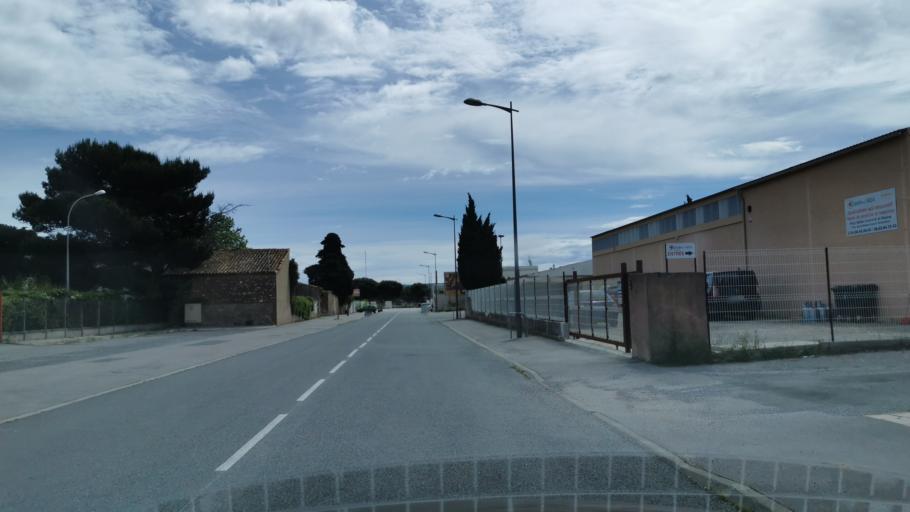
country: FR
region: Languedoc-Roussillon
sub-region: Departement de l'Aude
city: Narbonne
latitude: 43.1721
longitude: 2.9857
